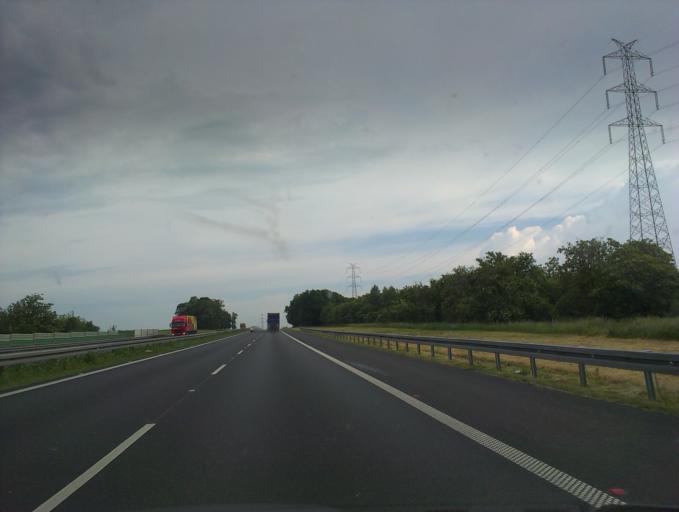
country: PL
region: Opole Voivodeship
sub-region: Powiat brzeski
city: Skarbimierz Osiedle
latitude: 50.8024
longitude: 17.3210
